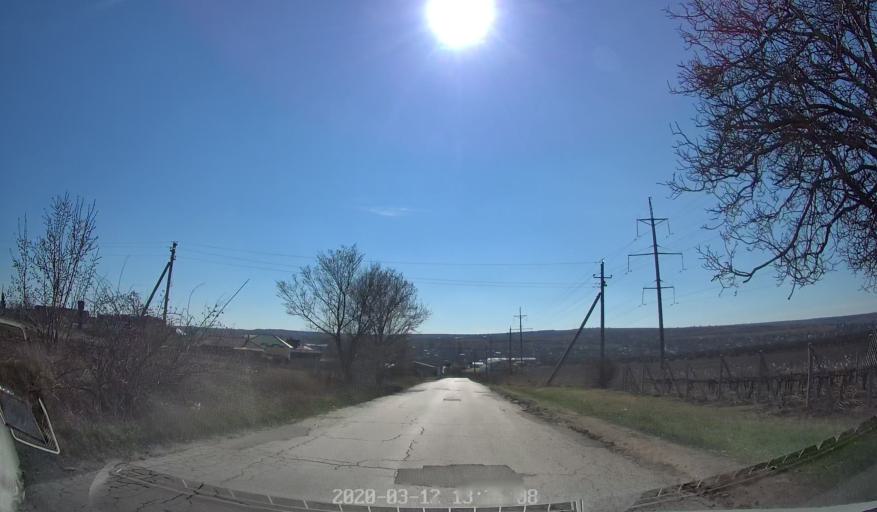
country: MD
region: Laloveni
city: Ialoveni
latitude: 46.9371
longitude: 28.8163
